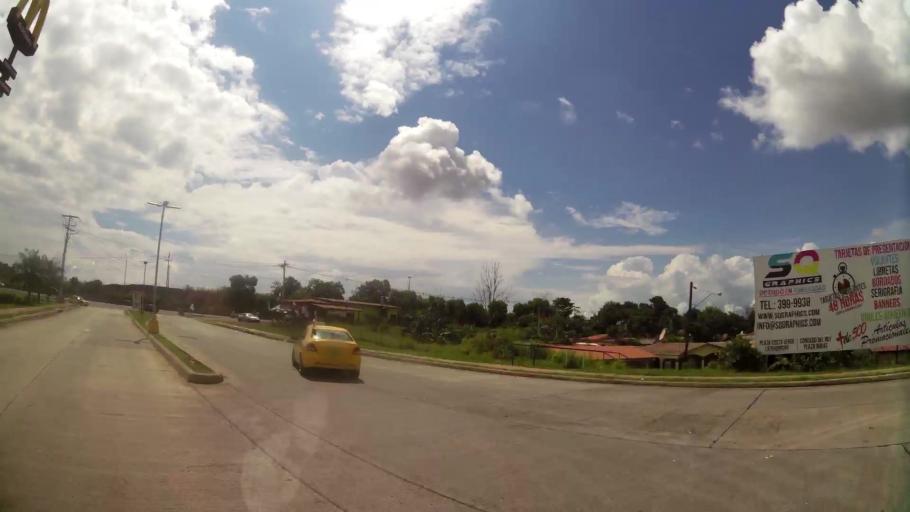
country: PA
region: Panama
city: Nuevo Arraijan
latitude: 8.9197
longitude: -79.7066
